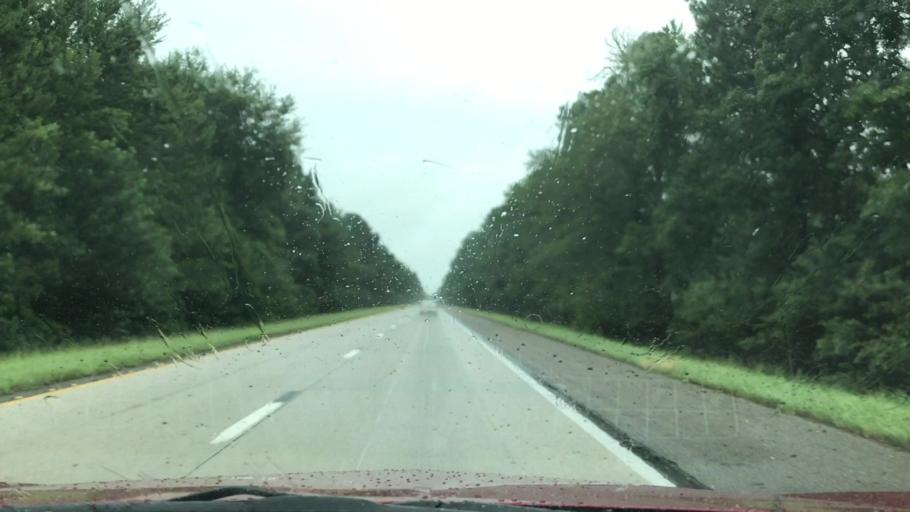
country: US
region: South Carolina
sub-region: Orangeburg County
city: Holly Hill
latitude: 33.2019
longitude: -80.4022
